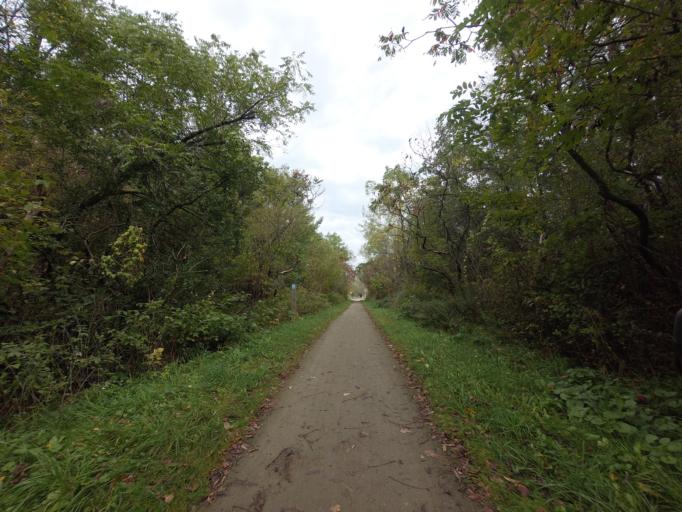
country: CA
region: Ontario
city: Ancaster
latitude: 43.2251
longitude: -80.0544
